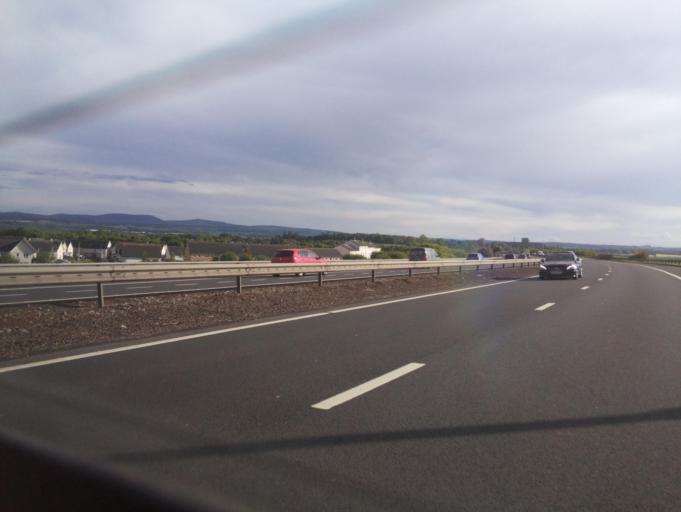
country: GB
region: Scotland
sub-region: Edinburgh
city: Kirkliston
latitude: 55.9629
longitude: -3.4121
